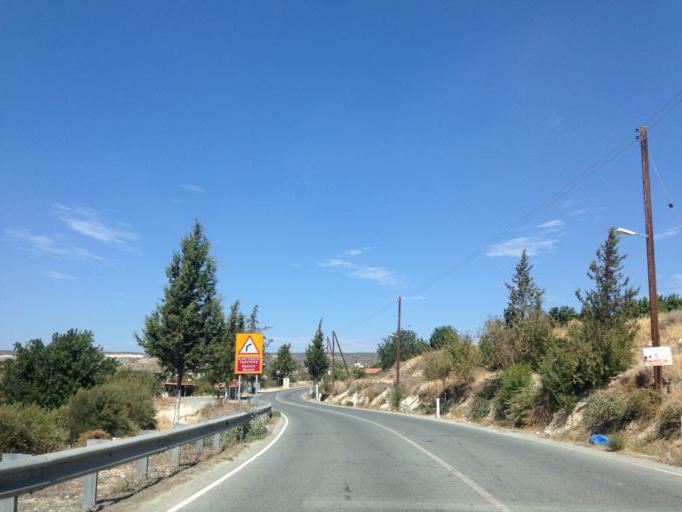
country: CY
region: Limassol
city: Pissouri
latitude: 34.6883
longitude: 32.7613
